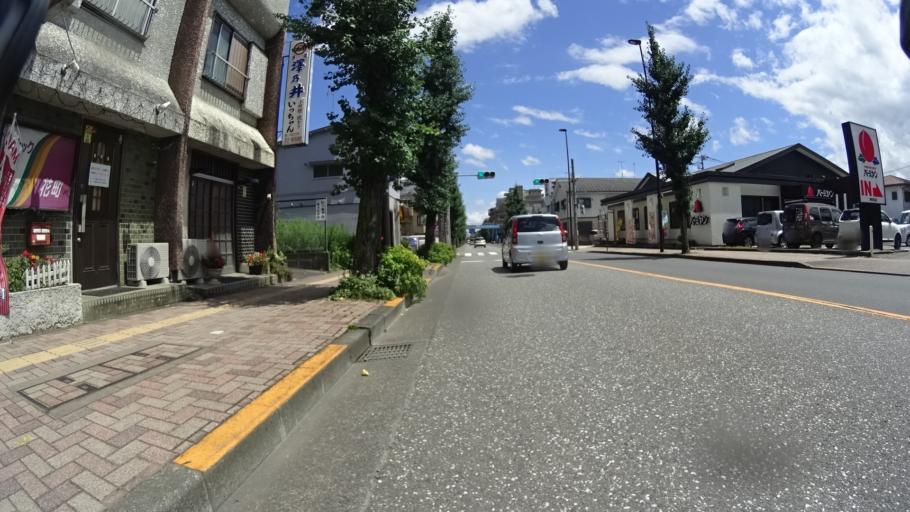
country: JP
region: Tokyo
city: Ome
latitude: 35.7821
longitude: 139.2855
